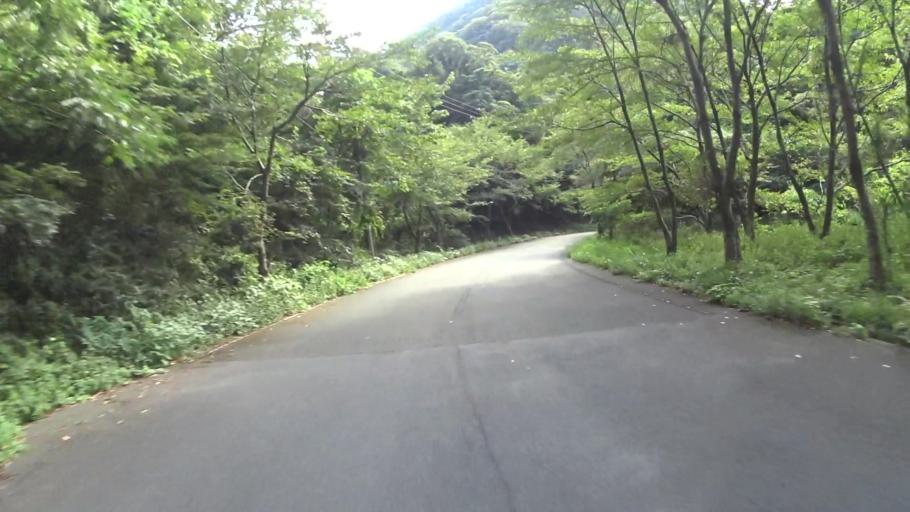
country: JP
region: Kyoto
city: Miyazu
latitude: 35.7705
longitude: 135.2256
